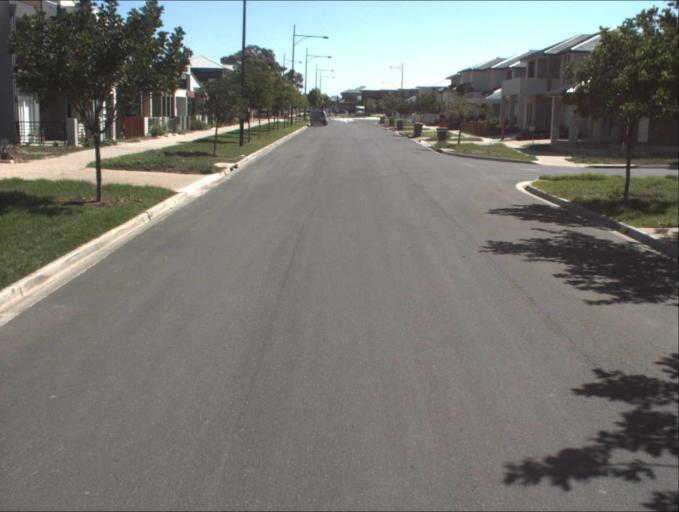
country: AU
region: South Australia
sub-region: Port Adelaide Enfield
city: Klemzig
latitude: -34.8615
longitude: 138.6280
